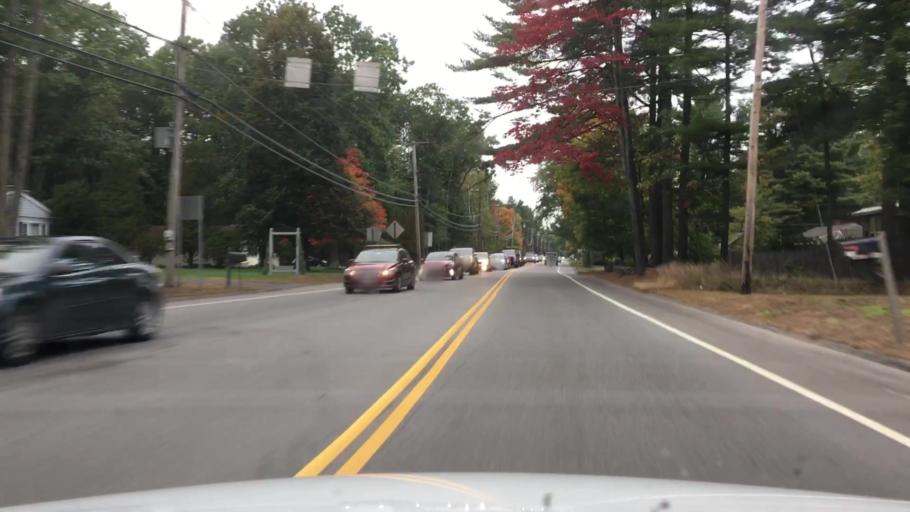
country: US
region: Maine
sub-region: Cumberland County
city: New Gloucester
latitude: 43.9031
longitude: -70.3460
